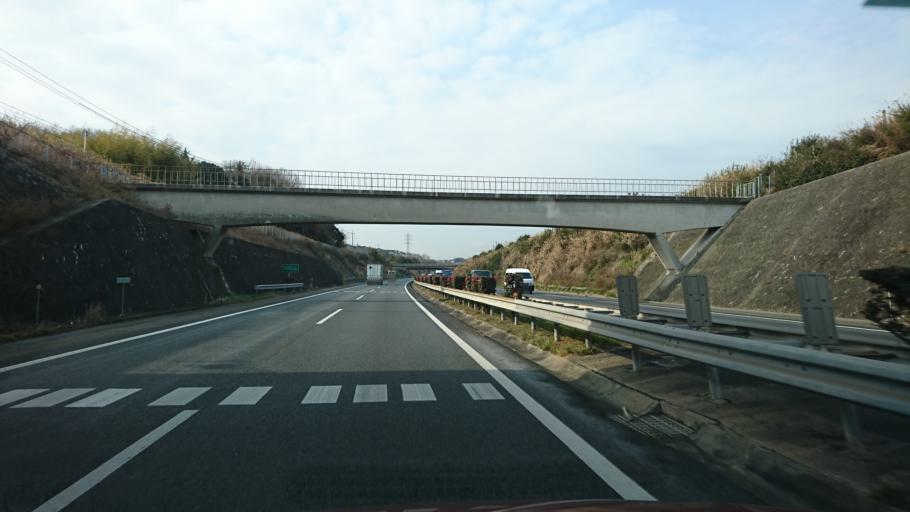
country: JP
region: Hiroshima
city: Kannabecho-yahiro
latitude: 34.5292
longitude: 133.4475
